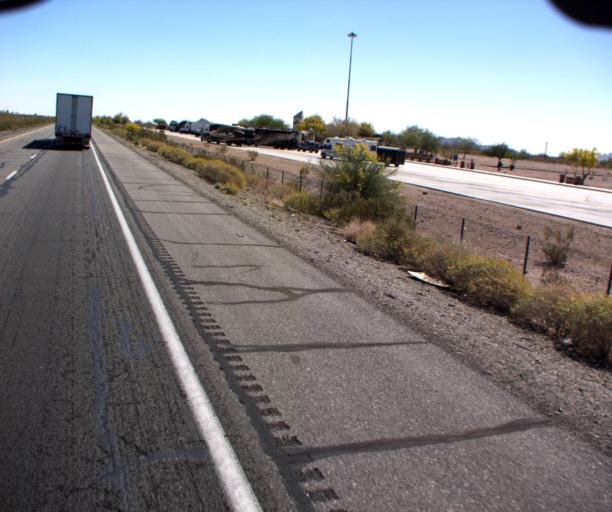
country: US
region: Arizona
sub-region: Maricopa County
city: Buckeye
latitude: 33.5207
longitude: -113.0719
